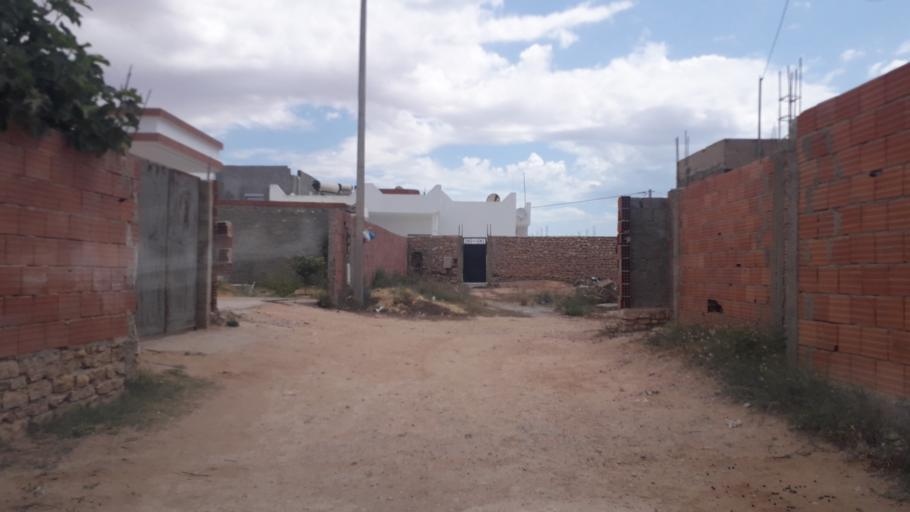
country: TN
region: Safaqis
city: Al Qarmadah
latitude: 34.8396
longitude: 10.7771
